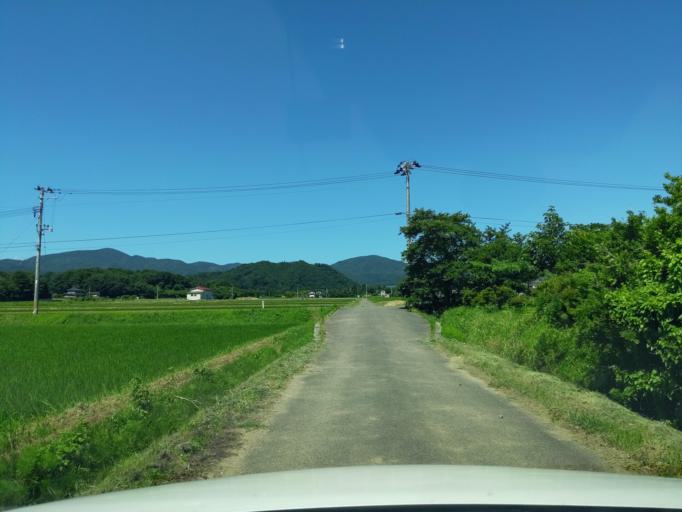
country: JP
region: Fukushima
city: Koriyama
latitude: 37.3914
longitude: 140.2771
